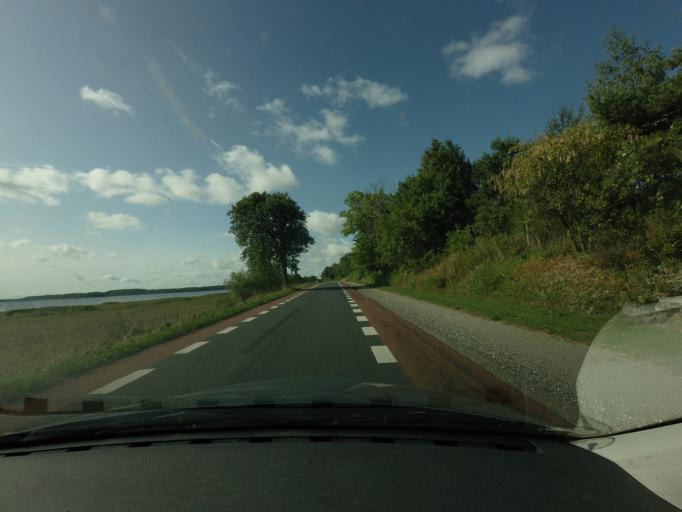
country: DK
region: Zealand
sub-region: Vordingborg Kommune
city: Praesto
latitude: 55.1629
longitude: 12.0224
